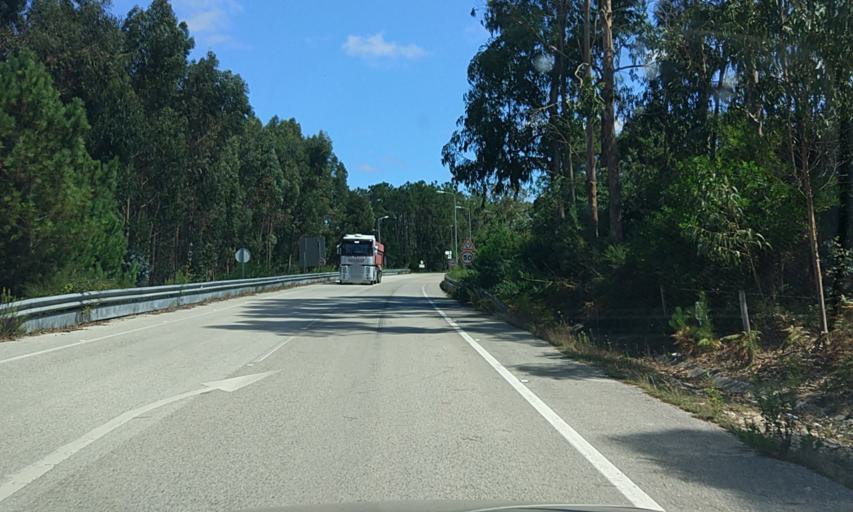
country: PT
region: Coimbra
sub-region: Mira
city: Mira
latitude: 40.3371
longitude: -8.7345
